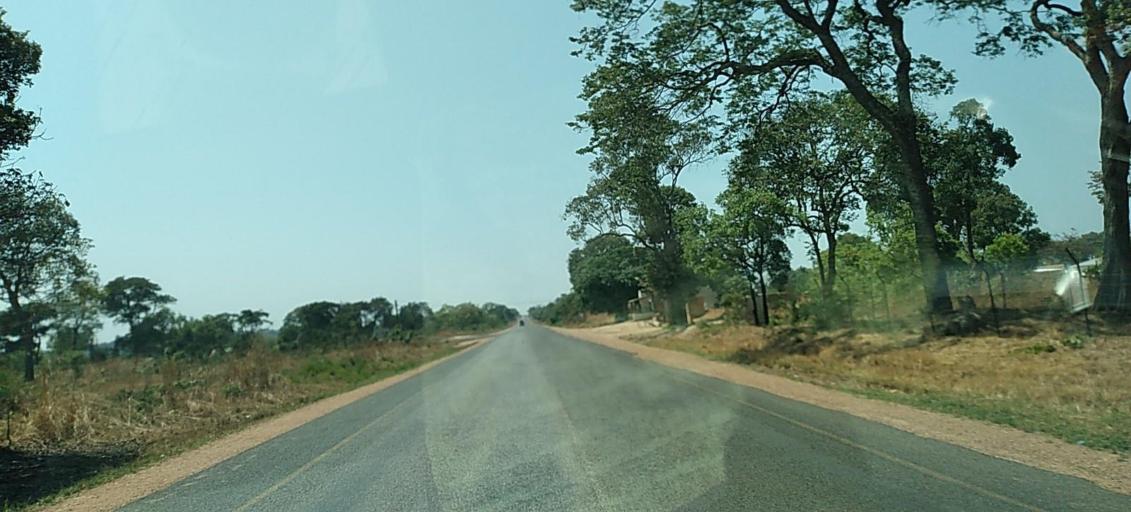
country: ZM
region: North-Western
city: Solwezi
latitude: -12.3000
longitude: 25.8308
